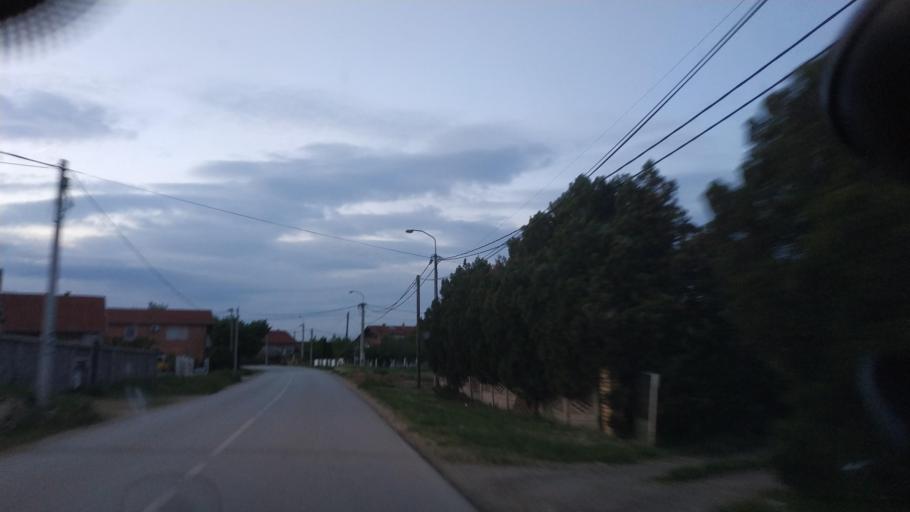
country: RS
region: Central Serbia
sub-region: Nisavski Okrug
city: Merosina
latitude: 43.2867
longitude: 21.7181
